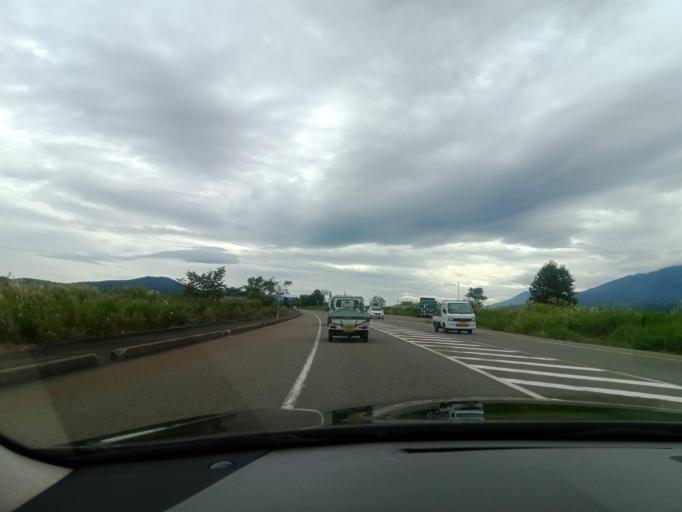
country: JP
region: Niigata
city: Arai
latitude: 37.0234
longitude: 138.2271
